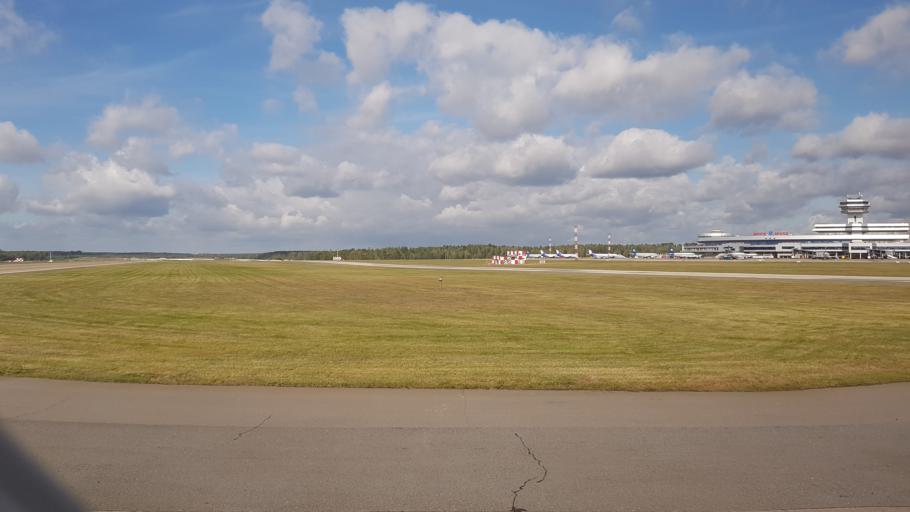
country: BY
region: Minsk
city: Smilavichy
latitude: 53.8831
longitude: 28.0310
